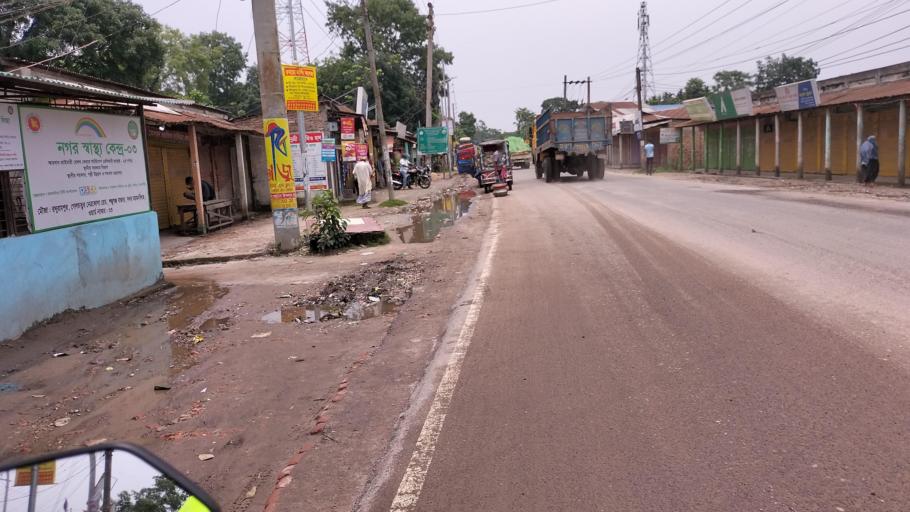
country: BD
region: Dhaka
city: Mymensingh
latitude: 24.7657
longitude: 90.4522
